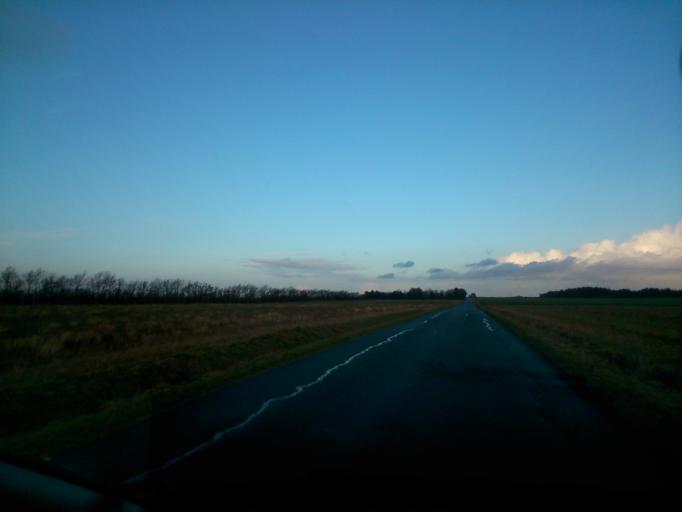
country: DK
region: Central Jutland
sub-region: Ringkobing-Skjern Kommune
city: Videbaek
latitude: 56.0357
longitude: 8.5633
